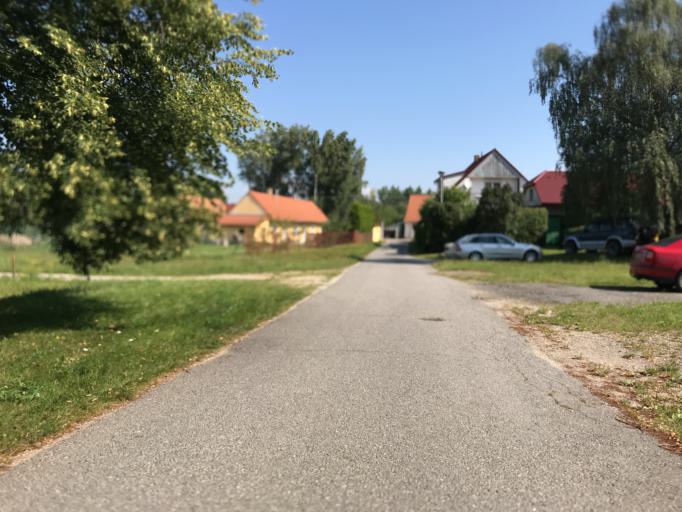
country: CZ
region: Jihocesky
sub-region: Okres Jindrichuv Hradec
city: Trebon
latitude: 49.0173
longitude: 14.7385
